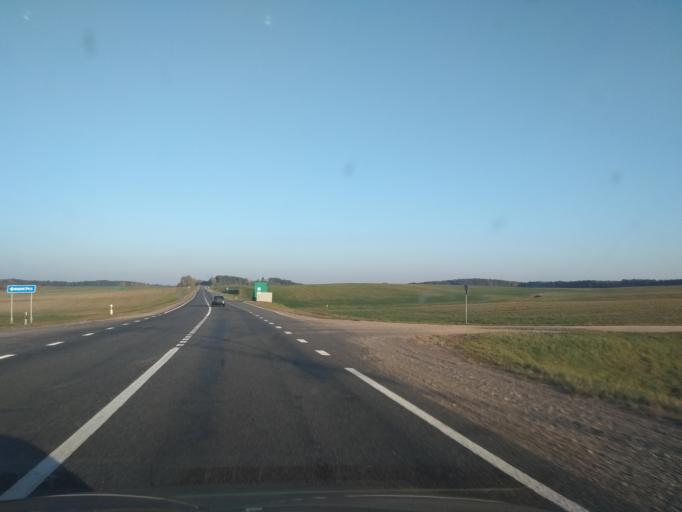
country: BY
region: Grodnenskaya
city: Zel'va
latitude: 53.1405
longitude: 24.6872
